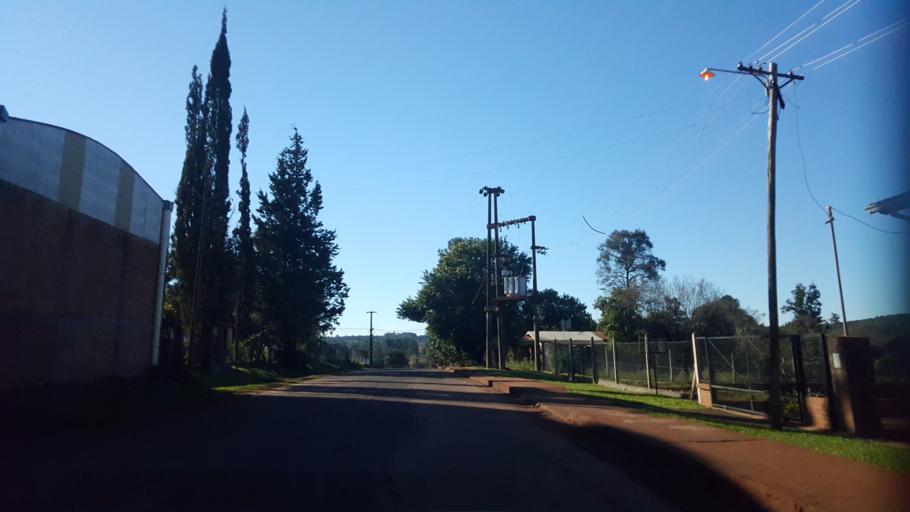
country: AR
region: Misiones
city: Jardin America
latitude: -27.0849
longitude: -55.2864
